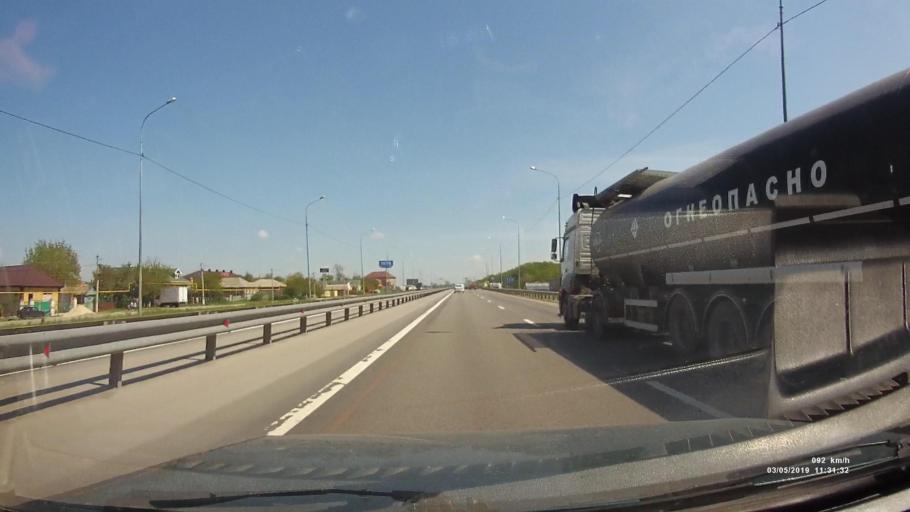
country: RU
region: Rostov
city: Bataysk
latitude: 47.1082
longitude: 39.8377
